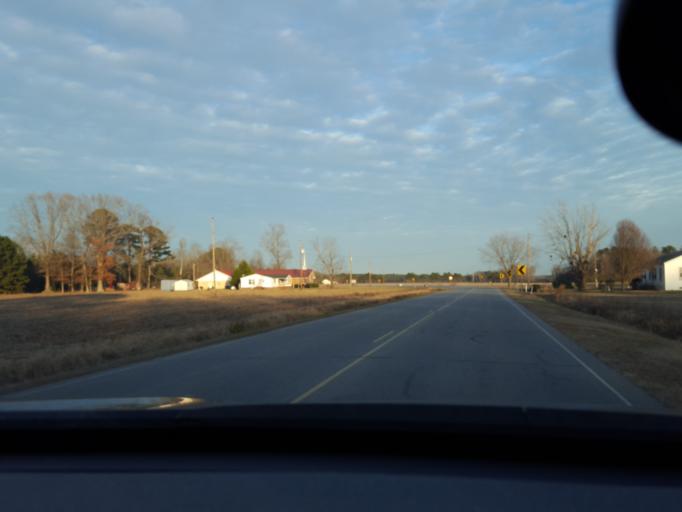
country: US
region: North Carolina
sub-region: Hertford County
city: Murfreesboro
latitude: 36.2718
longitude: -77.2253
